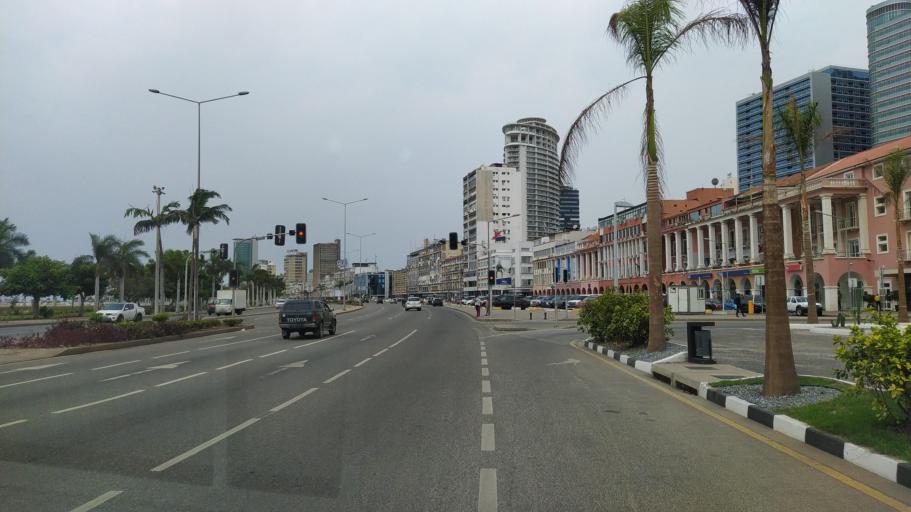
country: AO
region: Luanda
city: Luanda
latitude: -8.8098
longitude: 13.2354
